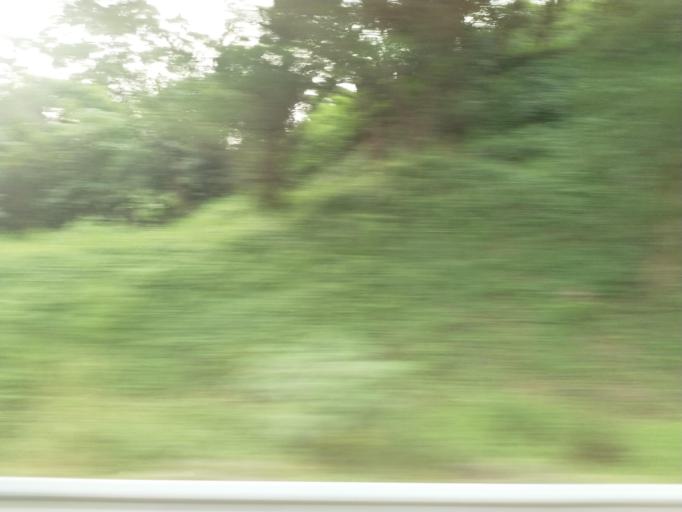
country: TW
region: Taiwan
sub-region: Pingtung
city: Pingtung
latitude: 22.7878
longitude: 120.4278
